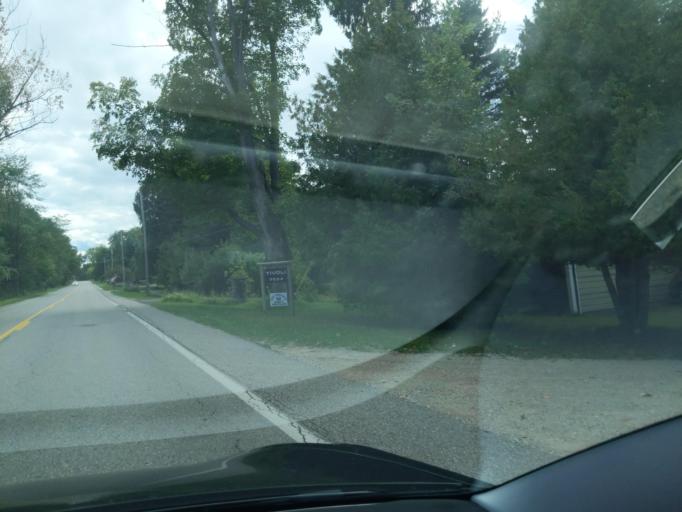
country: US
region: Michigan
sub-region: Kalkaska County
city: Rapid City
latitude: 44.9225
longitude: -85.2856
